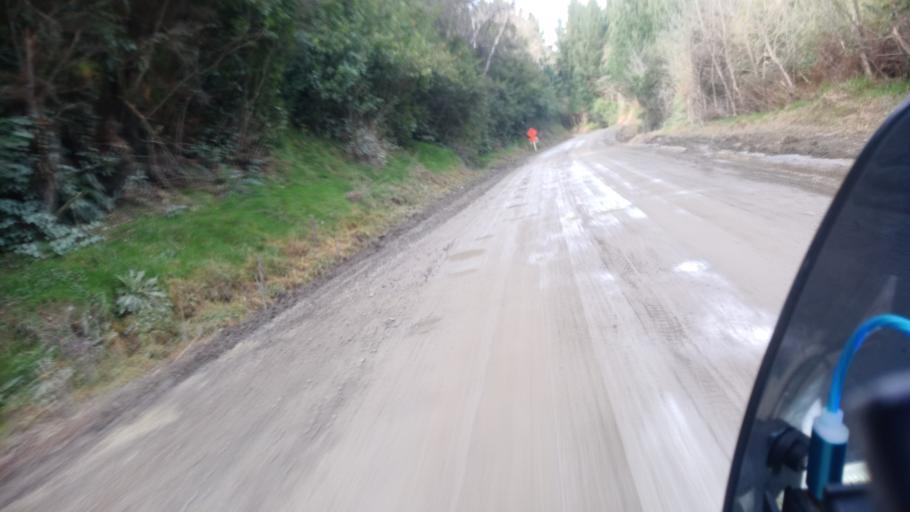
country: NZ
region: Gisborne
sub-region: Gisborne District
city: Gisborne
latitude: -38.1273
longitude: 178.1709
